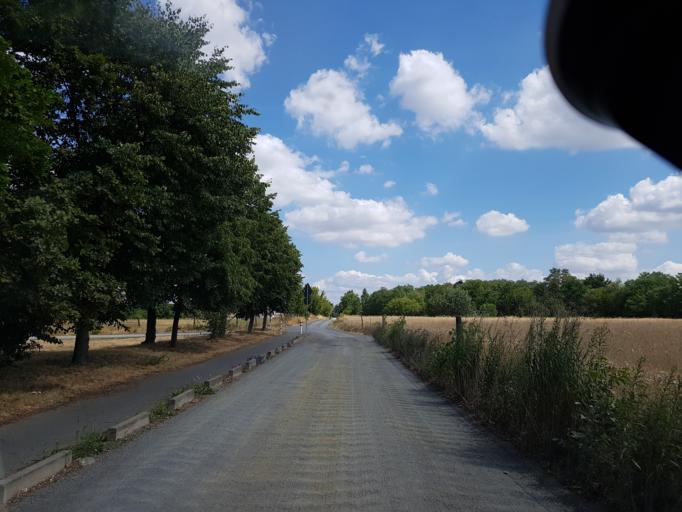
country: DE
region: Brandenburg
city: Cottbus
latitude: 51.7081
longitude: 14.3159
